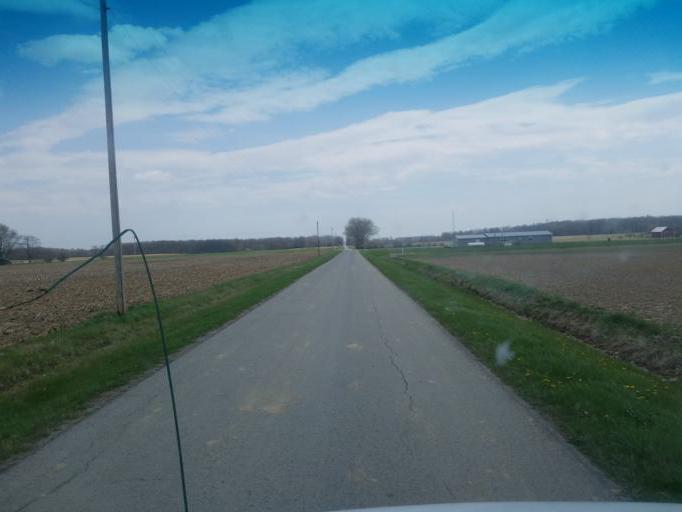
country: US
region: Ohio
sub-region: Hardin County
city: Forest
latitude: 40.7739
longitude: -83.4223
